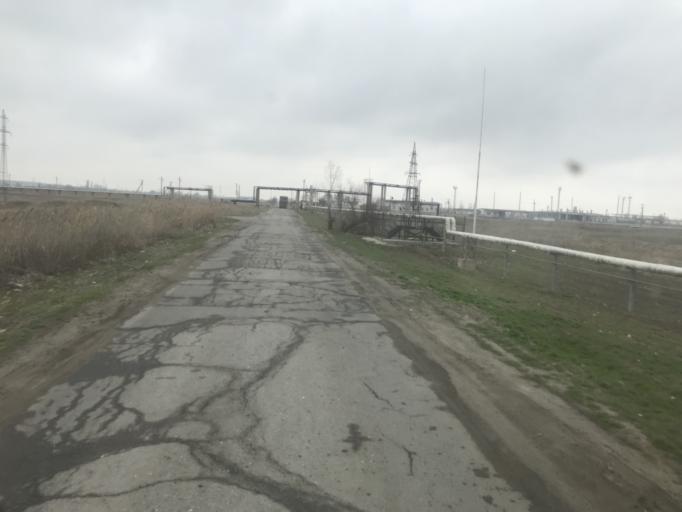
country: RU
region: Volgograd
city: Svetlyy Yar
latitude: 48.5127
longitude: 44.6355
